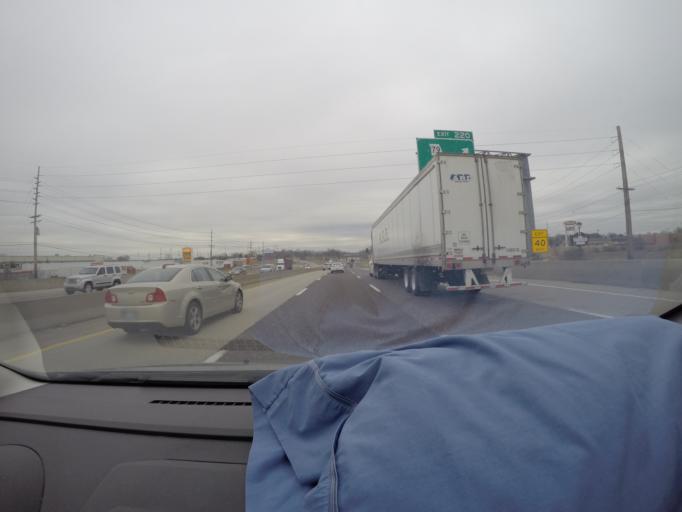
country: US
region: Missouri
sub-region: Saint Charles County
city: Saint Peters
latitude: 38.8024
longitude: -90.6568
